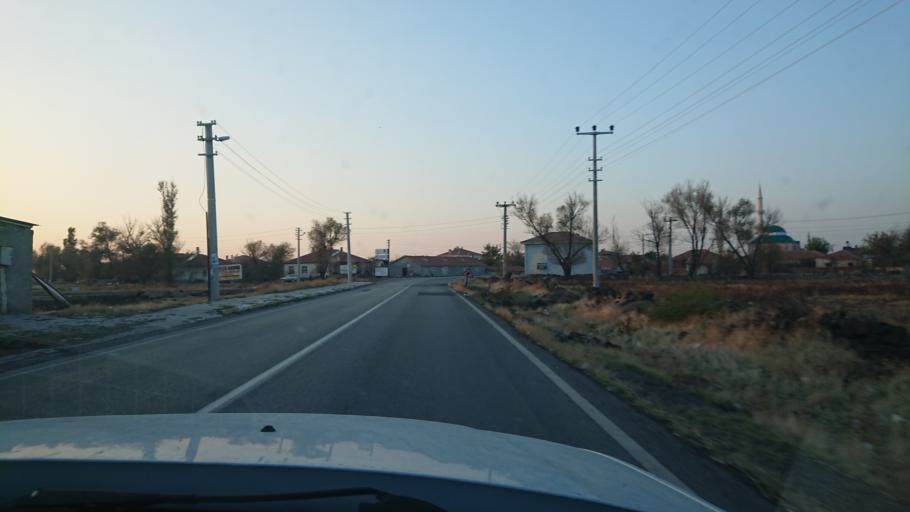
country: TR
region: Aksaray
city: Aksaray
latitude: 38.3167
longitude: 34.0542
